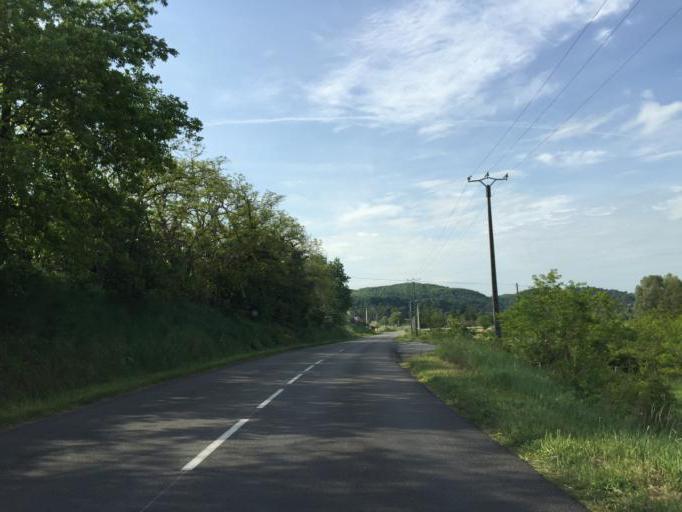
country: FR
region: Rhone-Alpes
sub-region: Departement de la Drome
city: Peyrins
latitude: 45.0862
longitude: 5.0305
